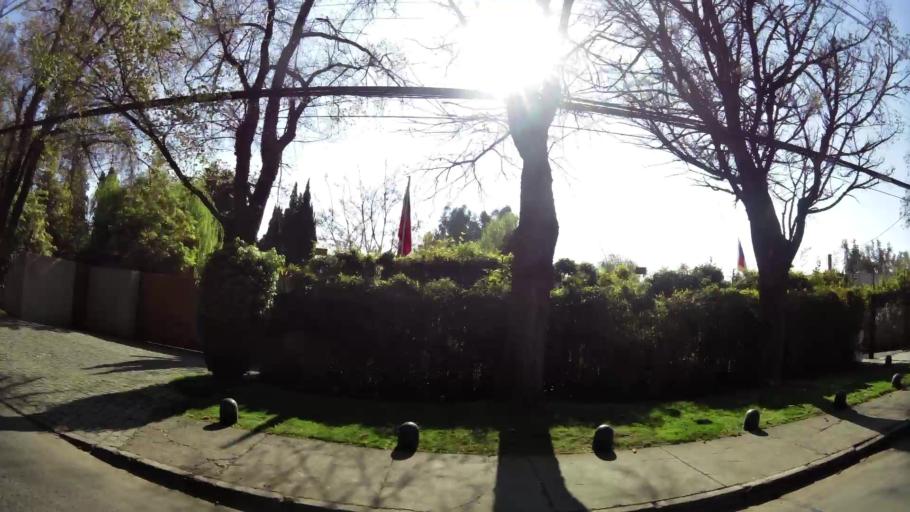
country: CL
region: Santiago Metropolitan
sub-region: Provincia de Santiago
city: Villa Presidente Frei, Nunoa, Santiago, Chile
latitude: -33.3916
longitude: -70.5212
